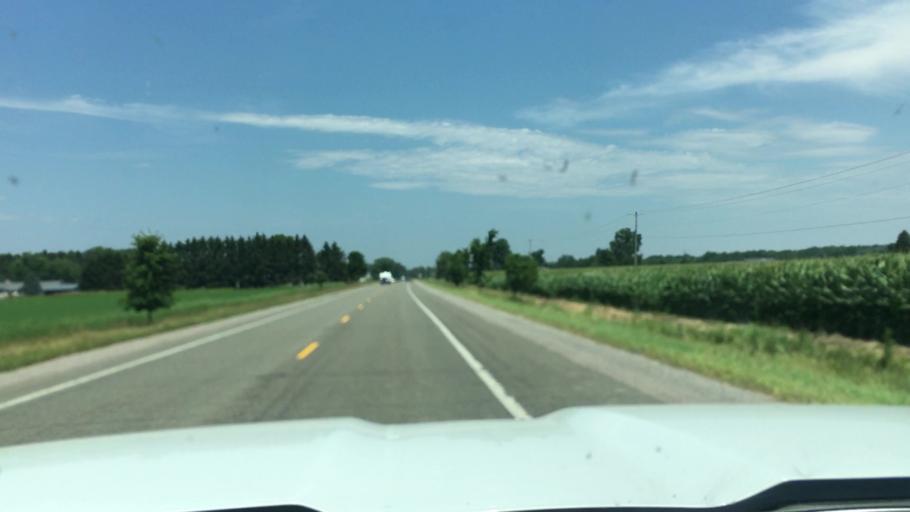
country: US
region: Michigan
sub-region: Saginaw County
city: Chesaning
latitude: 43.1975
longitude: -84.1693
